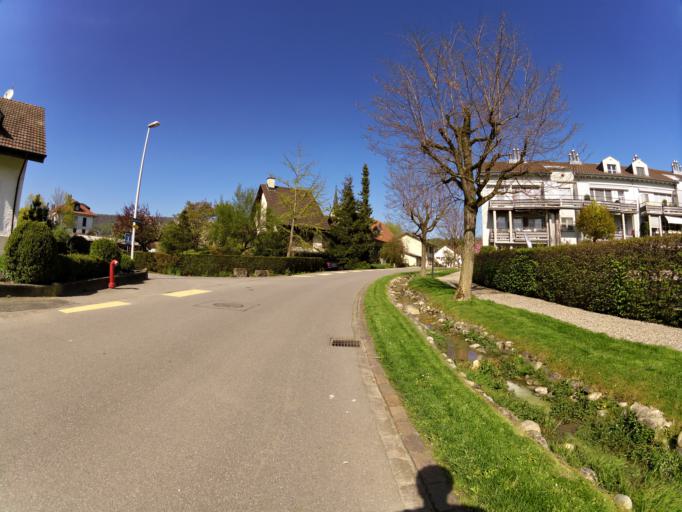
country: CH
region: Solothurn
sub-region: Bezirk Goesgen
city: Niedererlinsbach
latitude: 47.3953
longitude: 8.0057
